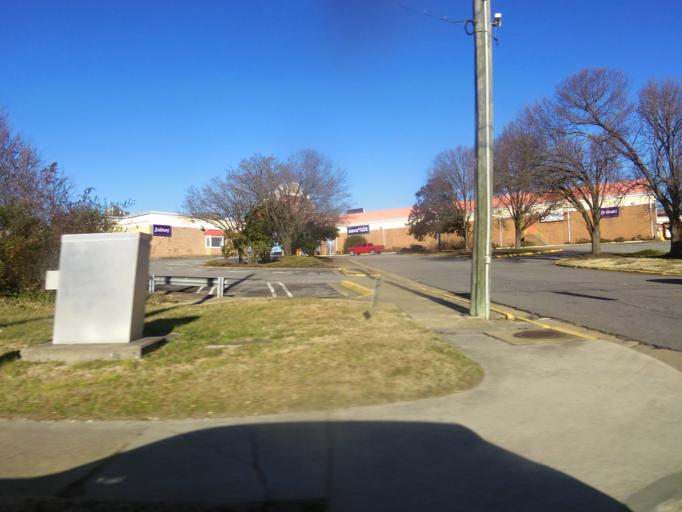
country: US
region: Virginia
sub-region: City of Hopewell
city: Hopewell
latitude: 37.2900
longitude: -77.2939
